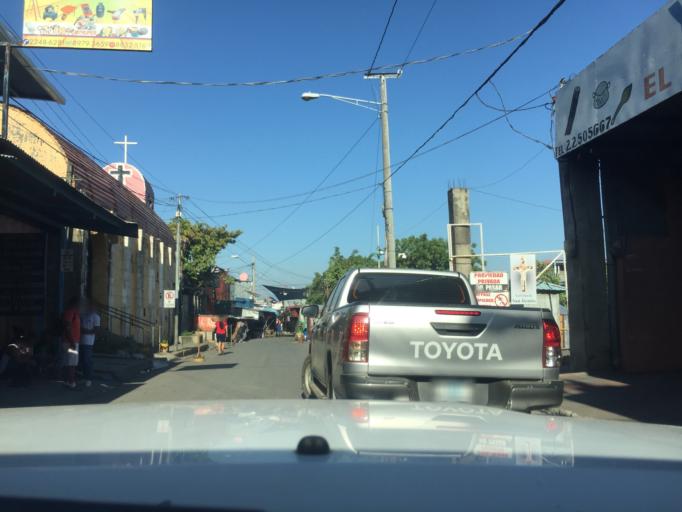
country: NI
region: Managua
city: Managua
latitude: 12.1513
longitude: -86.2585
